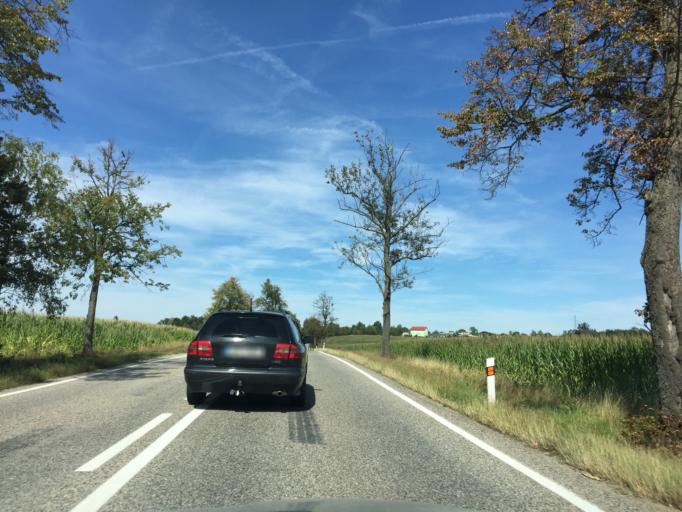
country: CZ
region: Jihocesky
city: Borek
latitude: 49.0593
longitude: 14.5154
